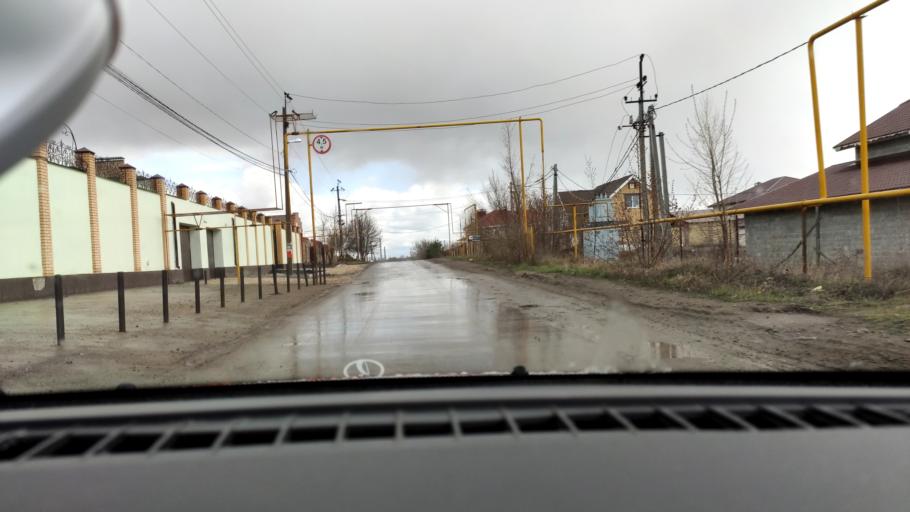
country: RU
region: Samara
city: Novosemeykino
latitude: 53.3273
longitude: 50.2903
